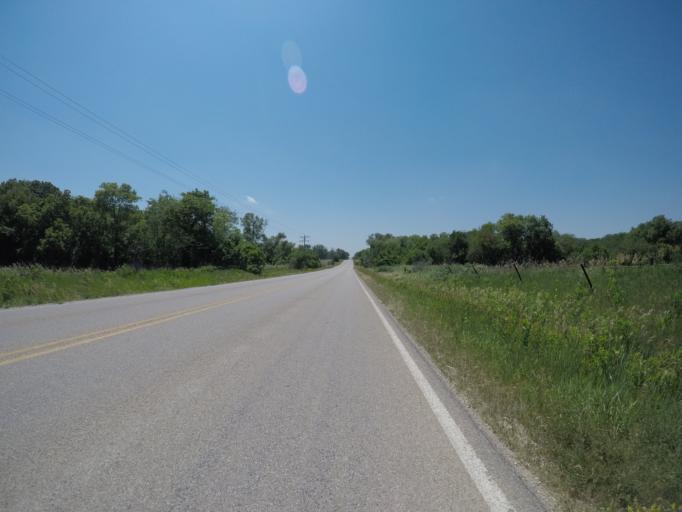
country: US
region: Kansas
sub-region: Riley County
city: Manhattan
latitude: 39.2459
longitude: -96.4453
